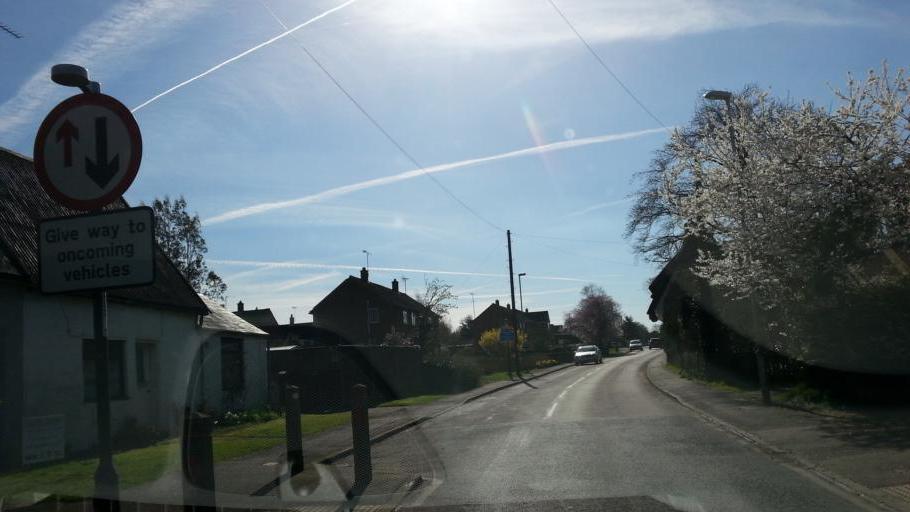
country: GB
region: England
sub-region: Cambridgeshire
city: Swavesey
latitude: 52.3169
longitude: 0.0111
